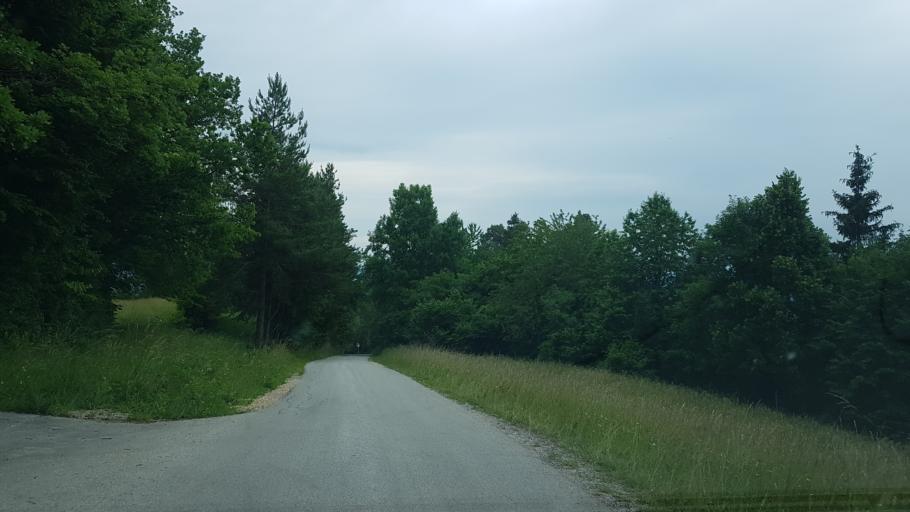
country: SI
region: Dobrna
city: Dobrna
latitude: 46.3593
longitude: 15.2419
